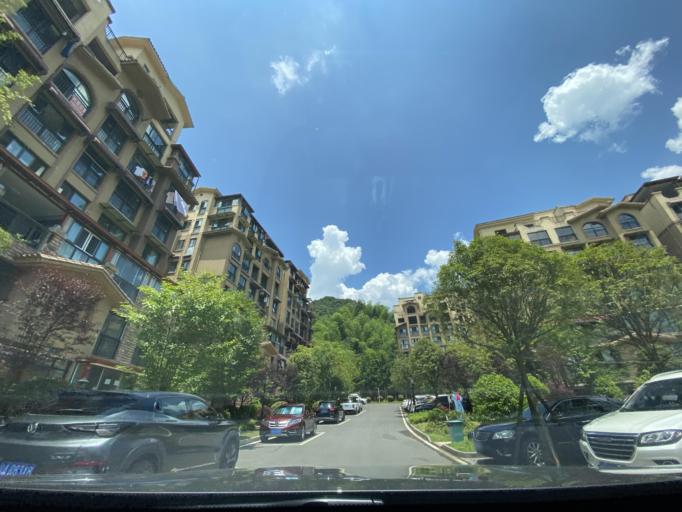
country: CN
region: Guizhou Sheng
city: Changqi
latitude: 28.5376
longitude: 105.9796
